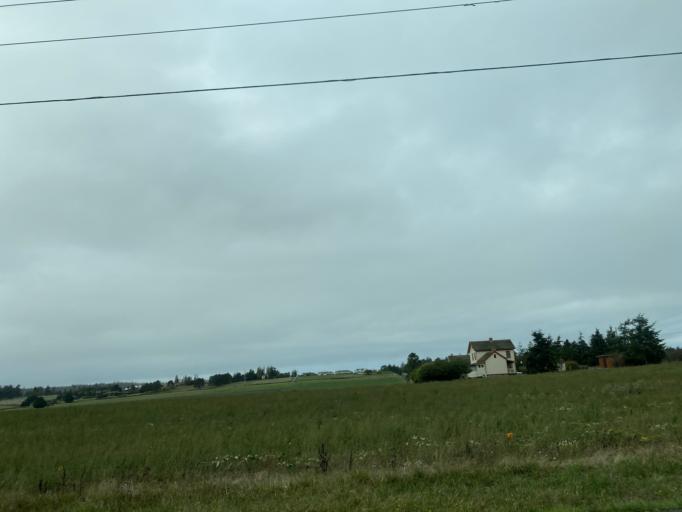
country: US
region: Washington
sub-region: Island County
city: Coupeville
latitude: 48.2114
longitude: -122.6930
